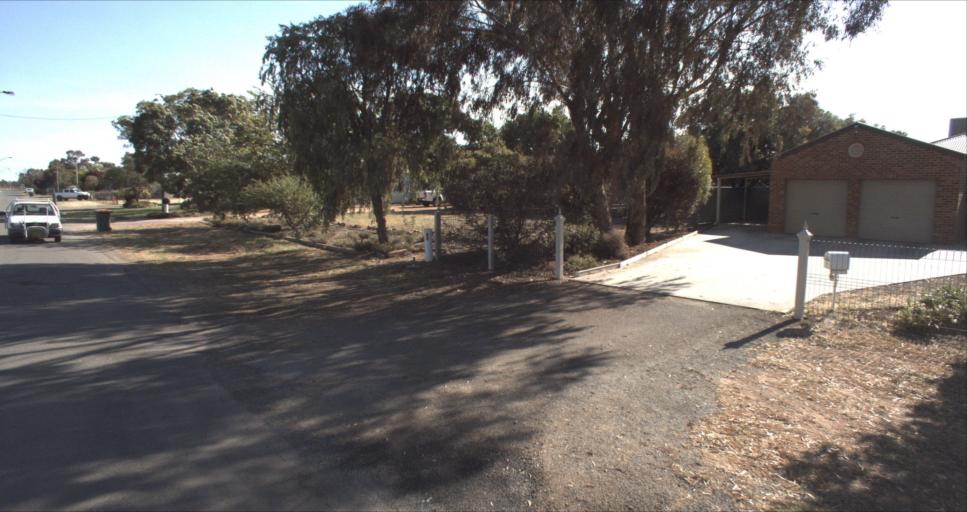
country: AU
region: New South Wales
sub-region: Leeton
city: Leeton
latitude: -34.5472
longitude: 146.4144
